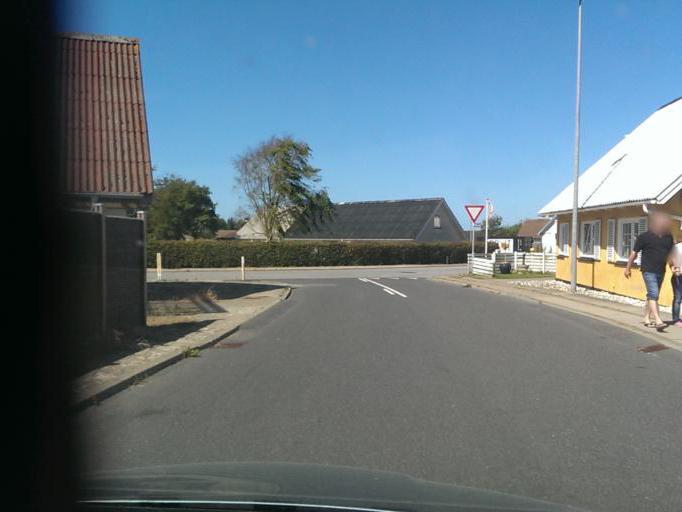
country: DK
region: North Denmark
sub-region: Jammerbugt Kommune
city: Pandrup
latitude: 57.3154
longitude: 9.7110
